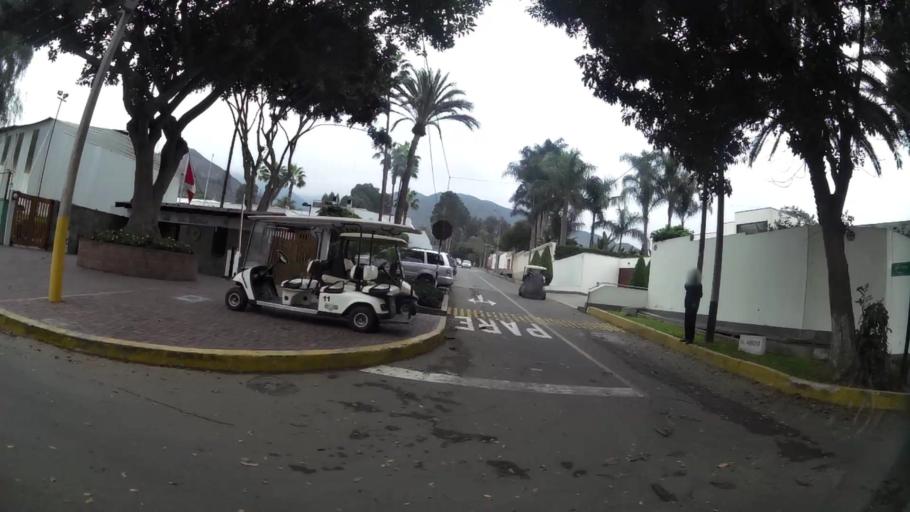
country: PE
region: Lima
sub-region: Lima
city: La Molina
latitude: -12.0755
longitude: -76.9080
